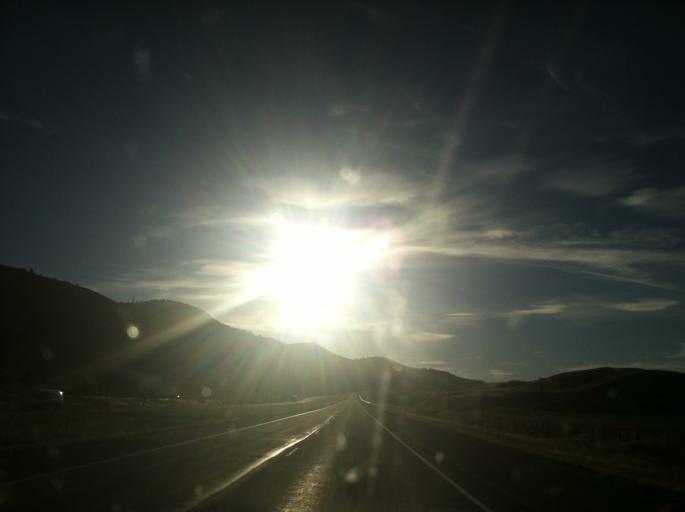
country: US
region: Montana
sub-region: Granite County
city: Philipsburg
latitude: 46.6974
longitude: -113.2142
